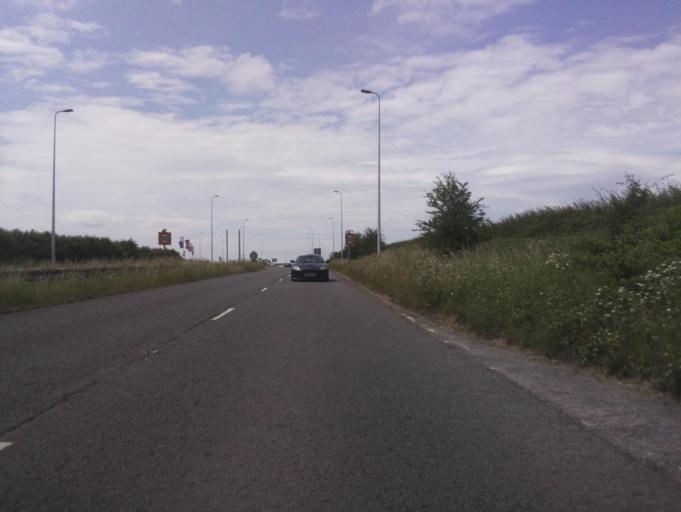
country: GB
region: Wales
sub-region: Vale of Glamorgan
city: Penllyn
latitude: 51.4659
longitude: -3.4652
